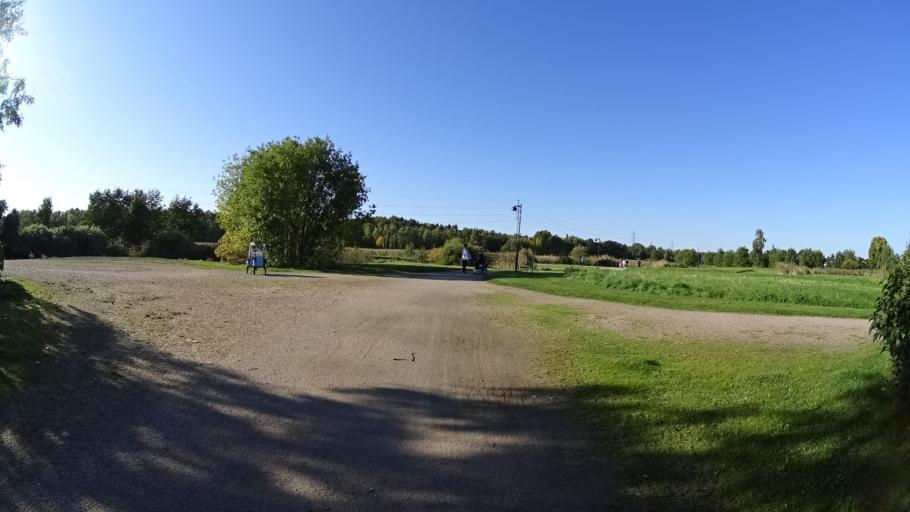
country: FI
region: Uusimaa
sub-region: Helsinki
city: Helsinki
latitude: 60.1974
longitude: 24.8931
